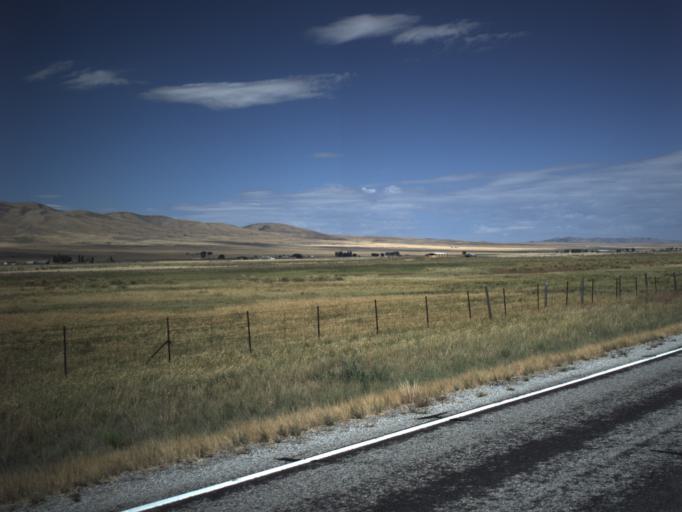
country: US
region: Utah
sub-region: Box Elder County
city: Tremonton
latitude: 41.7558
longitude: -112.4347
